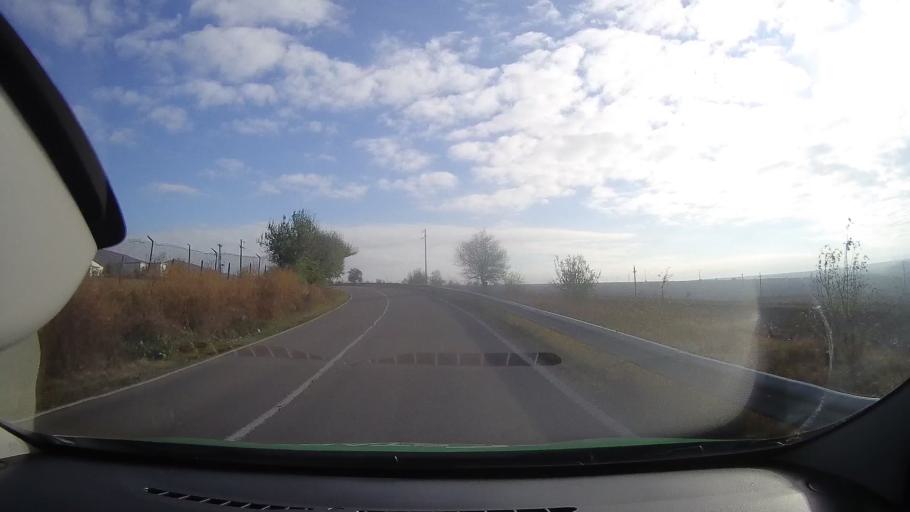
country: RO
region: Tulcea
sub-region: Comuna Bestepe
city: Bestepe
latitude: 45.0816
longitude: 29.0269
